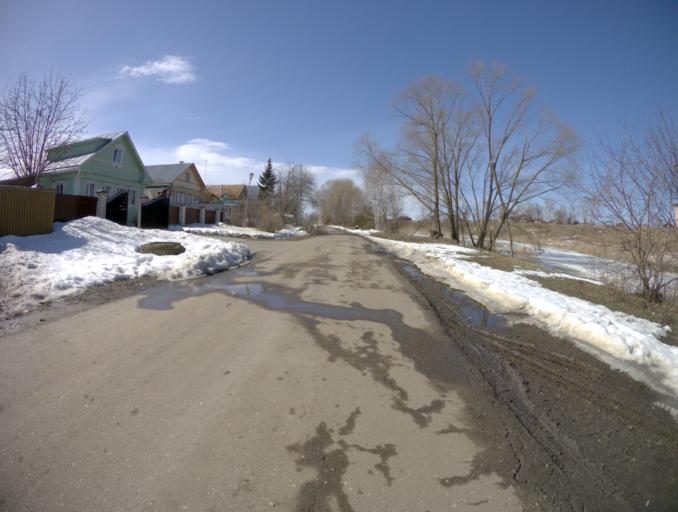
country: RU
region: Vladimir
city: Suzdal'
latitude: 56.4320
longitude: 40.4368
